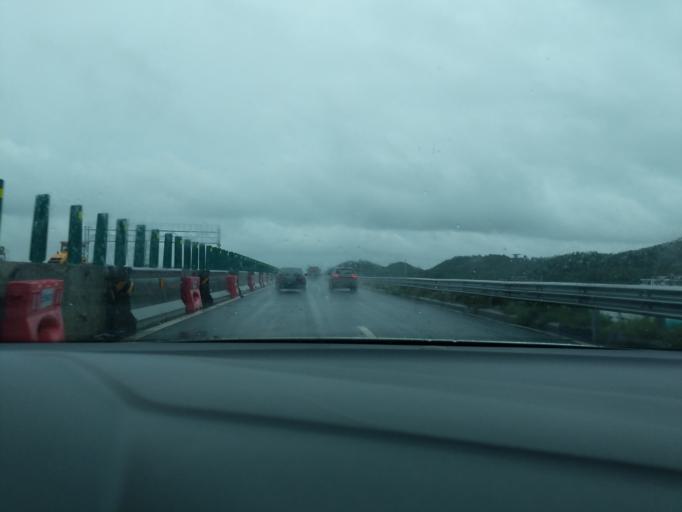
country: CN
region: Guangdong
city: Yueshan
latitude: 22.4630
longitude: 112.7163
